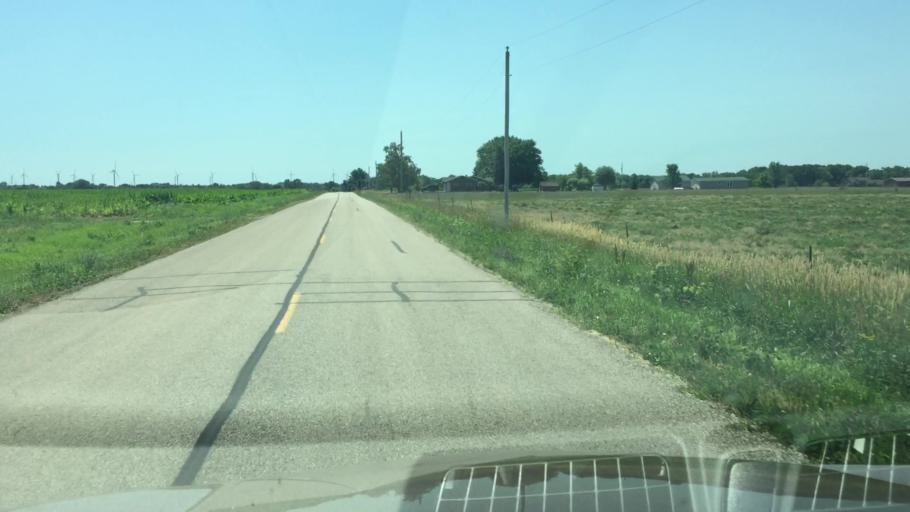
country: US
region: Wisconsin
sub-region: Fond du Lac County
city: Saint Peter
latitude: 43.9506
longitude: -88.3115
